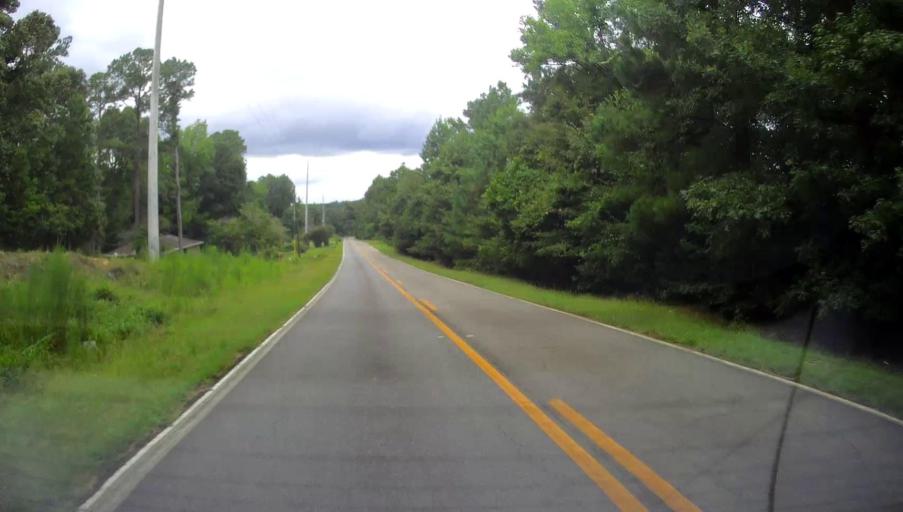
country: US
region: Georgia
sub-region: Bibb County
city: Macon
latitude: 32.7977
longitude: -83.5277
